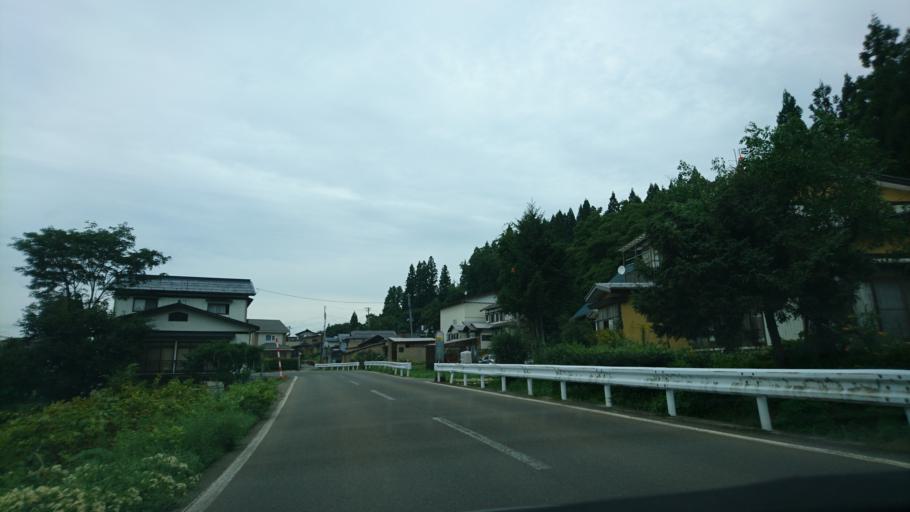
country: JP
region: Akita
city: Yuzawa
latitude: 39.1415
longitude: 140.5774
